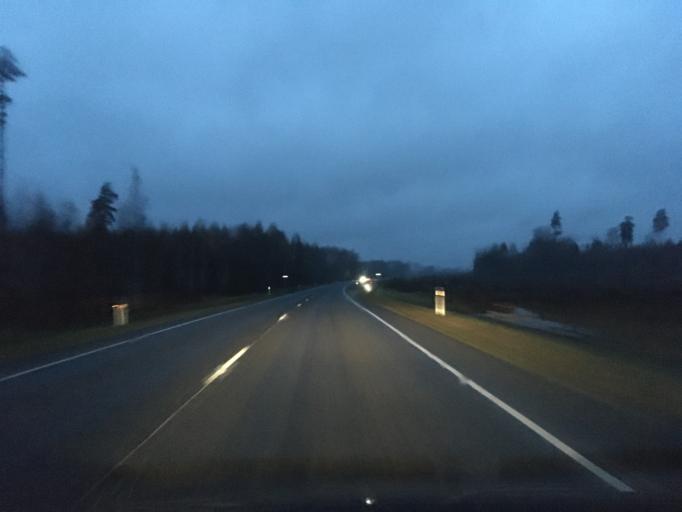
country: EE
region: Harju
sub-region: Nissi vald
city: Turba
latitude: 58.9706
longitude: 24.0639
